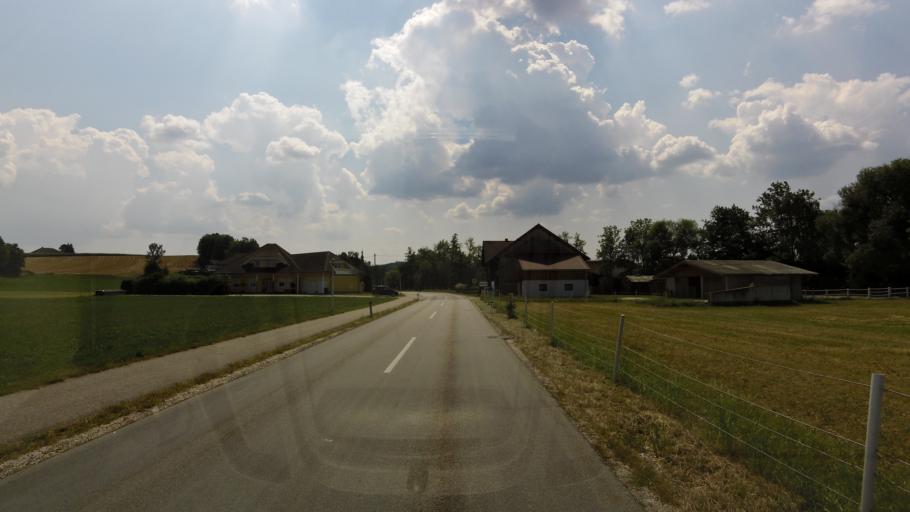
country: AT
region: Upper Austria
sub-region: Politischer Bezirk Ried im Innkreis
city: Waldzell
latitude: 48.1412
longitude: 13.4244
